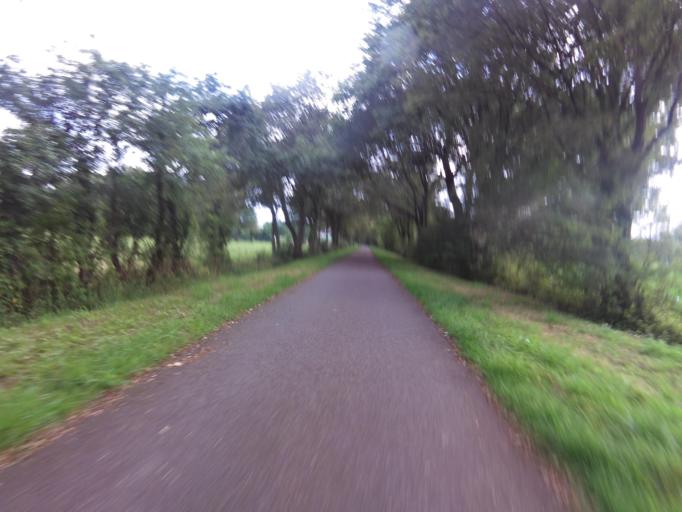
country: FR
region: Brittany
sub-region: Departement du Morbihan
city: Malestroit
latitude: 47.8267
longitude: -2.4198
